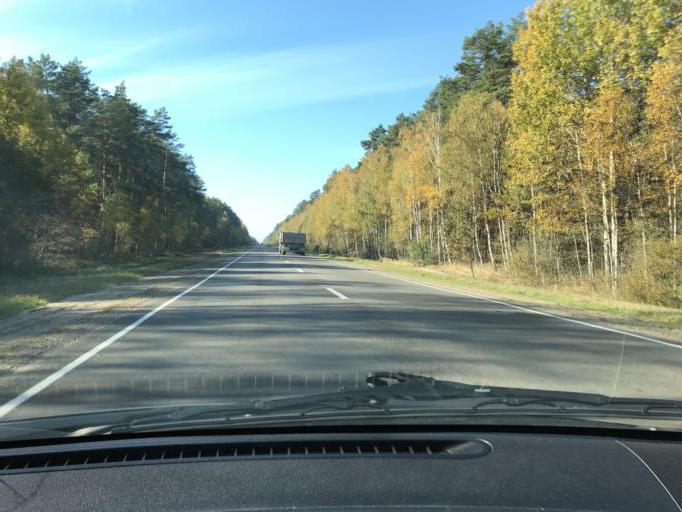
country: BY
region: Brest
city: Asnyezhytsy
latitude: 52.2446
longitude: 26.2265
